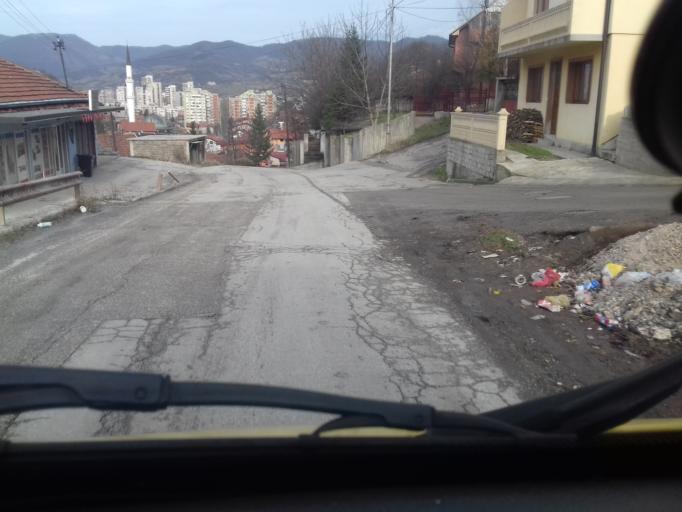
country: BA
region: Federation of Bosnia and Herzegovina
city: Zenica
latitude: 44.1880
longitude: 17.9073
